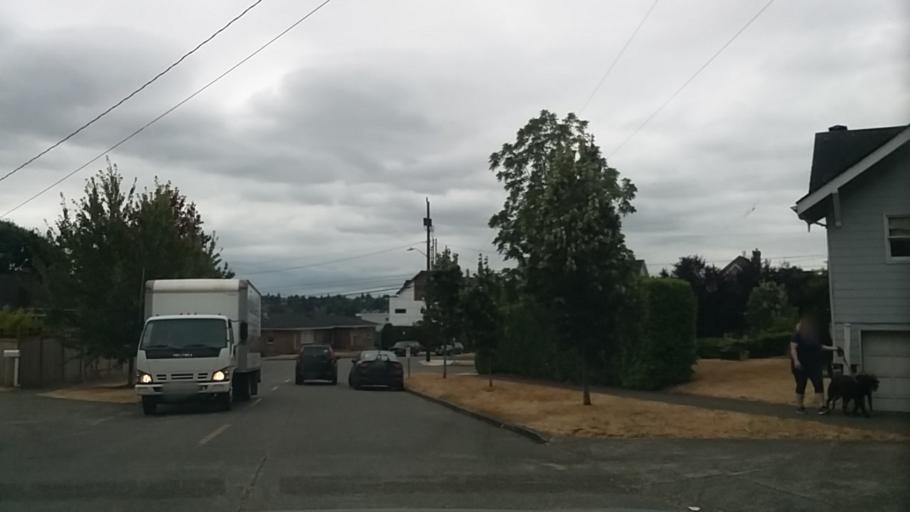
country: US
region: Washington
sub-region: King County
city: Shoreline
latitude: 47.6837
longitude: -122.3469
